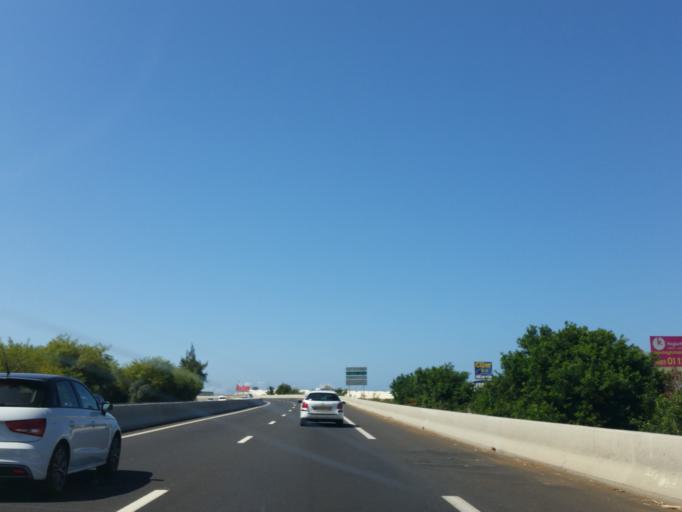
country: RE
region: Reunion
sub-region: Reunion
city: Saint-Louis
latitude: -21.2896
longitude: 55.4012
